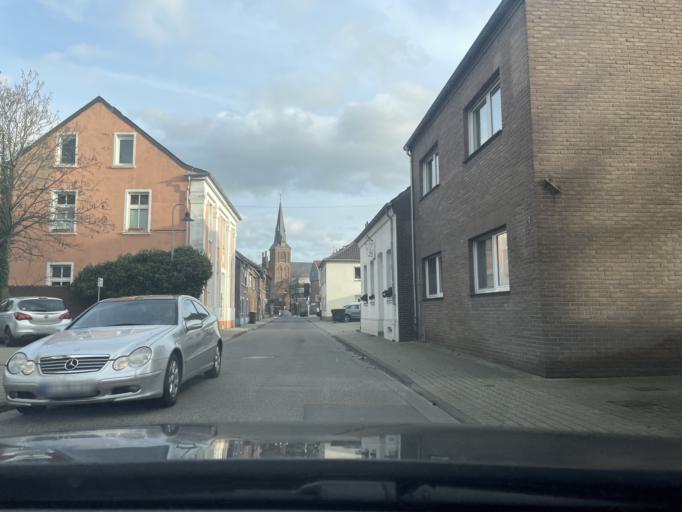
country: DE
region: North Rhine-Westphalia
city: Kempen
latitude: 51.3846
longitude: 6.4490
